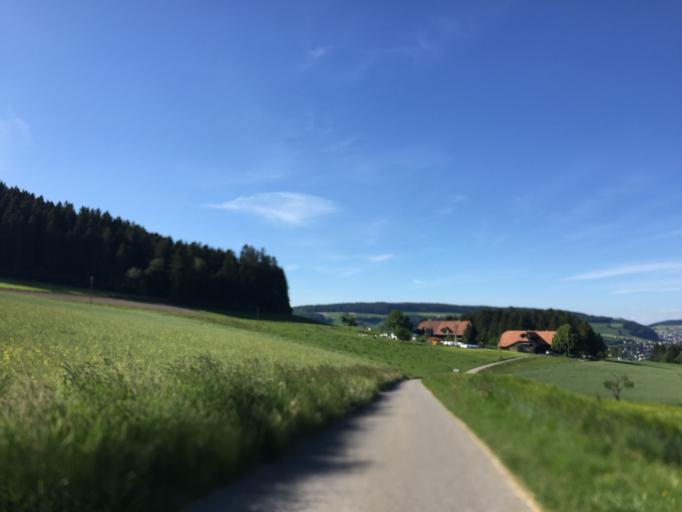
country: CH
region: Bern
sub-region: Bern-Mittelland District
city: Konolfingen
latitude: 46.8605
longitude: 7.6164
